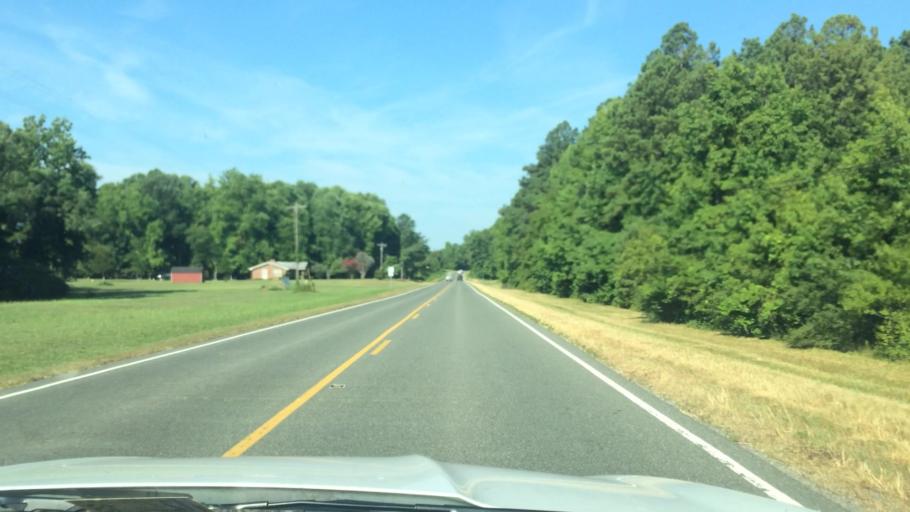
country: US
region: Virginia
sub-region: Northumberland County
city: Heathsville
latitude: 37.8510
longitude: -76.5914
